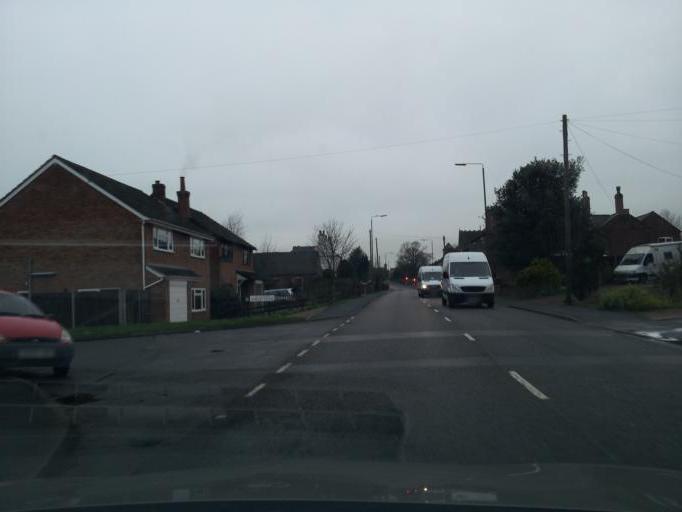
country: GB
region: England
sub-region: Derbyshire
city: Netherseal
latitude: 52.7334
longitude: -1.5634
